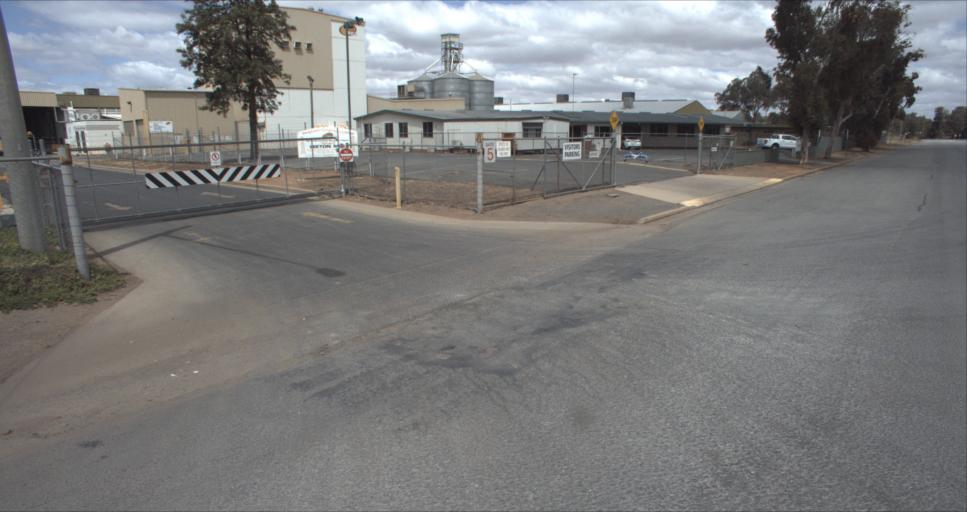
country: AU
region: New South Wales
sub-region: Leeton
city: Leeton
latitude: -34.5565
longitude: 146.3929
